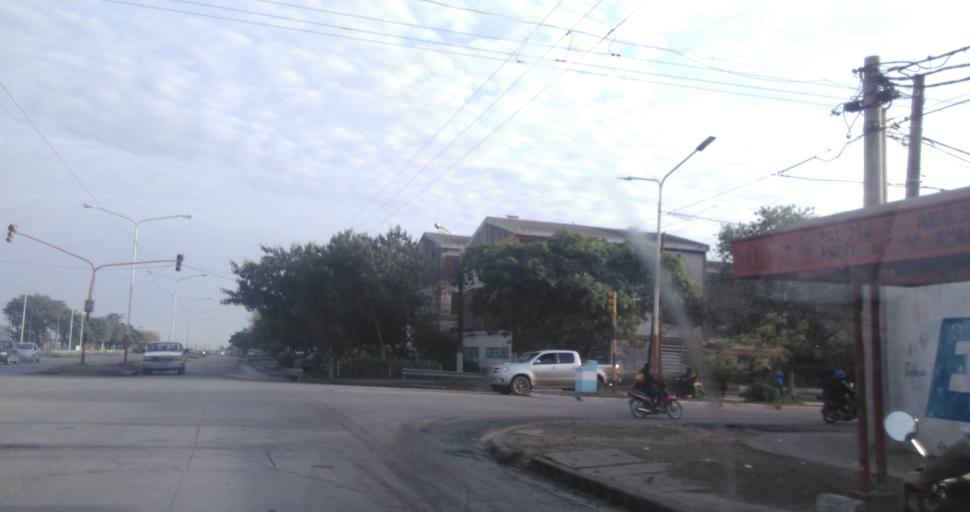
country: AR
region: Chaco
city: Resistencia
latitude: -27.4705
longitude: -59.0077
